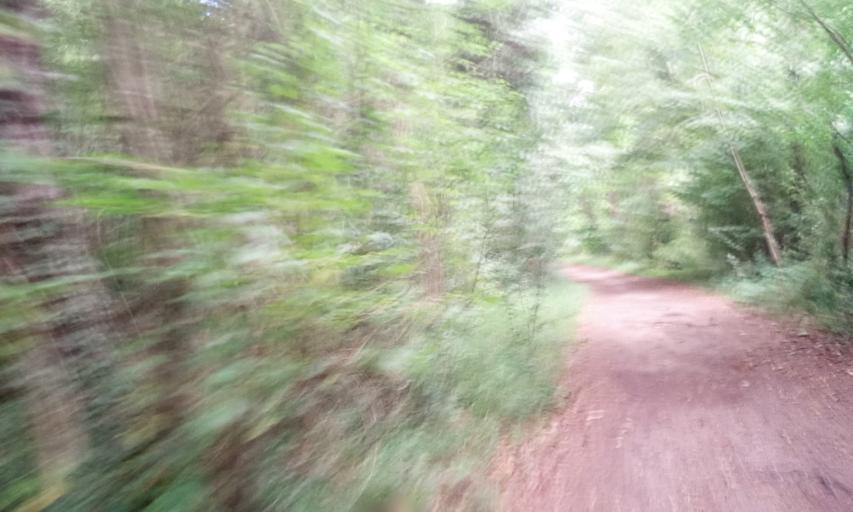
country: FR
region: Lower Normandy
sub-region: Departement du Calvados
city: Bellengreville
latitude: 49.1166
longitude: -0.2033
